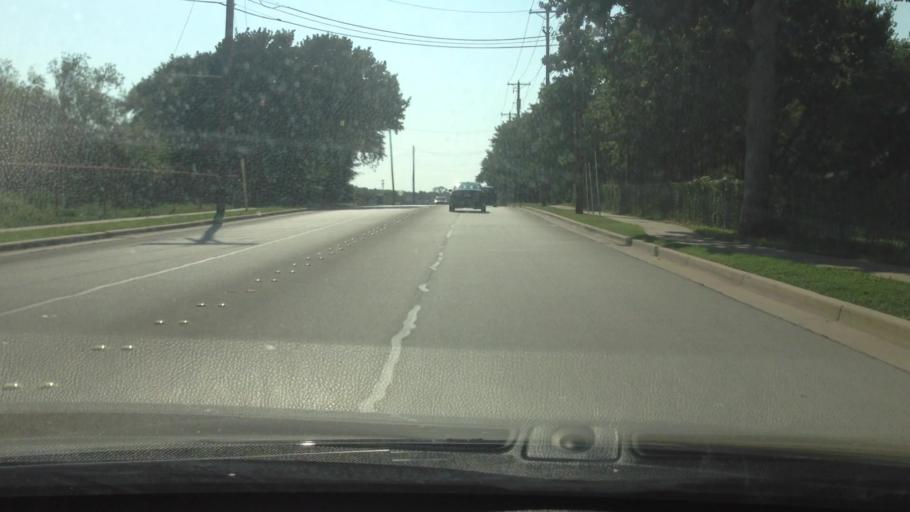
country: US
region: Texas
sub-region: Tarrant County
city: Colleyville
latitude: 32.8840
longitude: -97.1964
